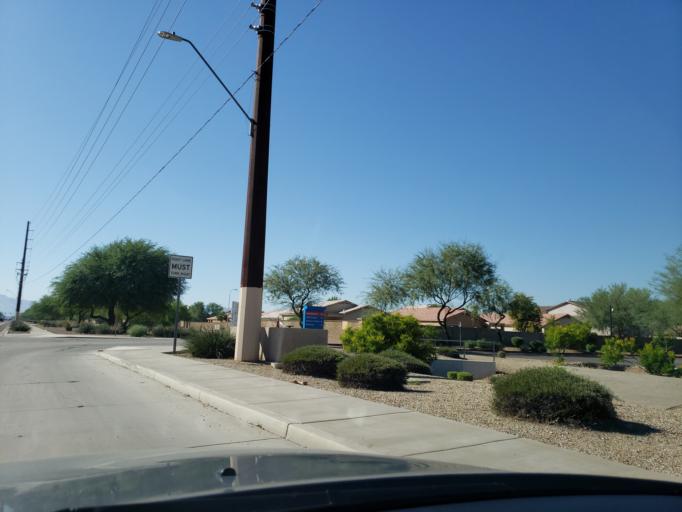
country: US
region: Arizona
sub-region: Maricopa County
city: Tolleson
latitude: 33.4774
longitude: -112.2553
